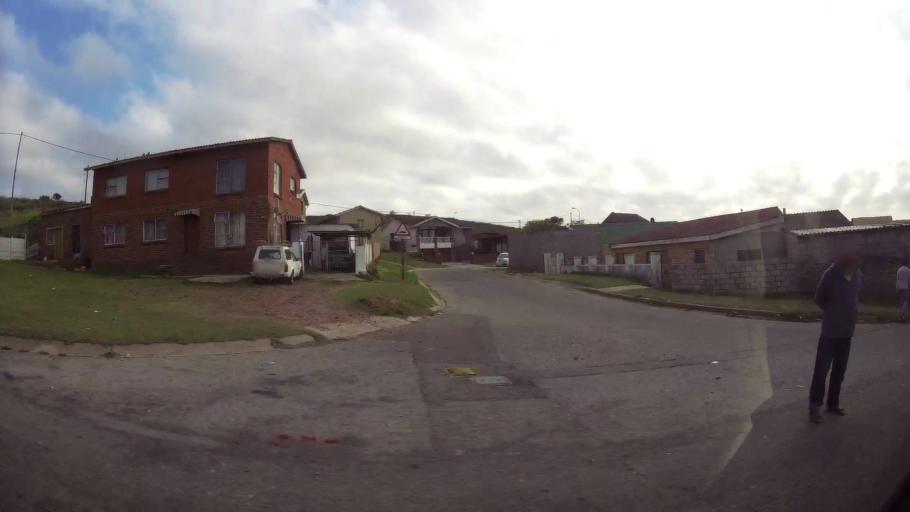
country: ZA
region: Eastern Cape
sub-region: Nelson Mandela Bay Metropolitan Municipality
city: Port Elizabeth
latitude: -33.9161
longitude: 25.5433
